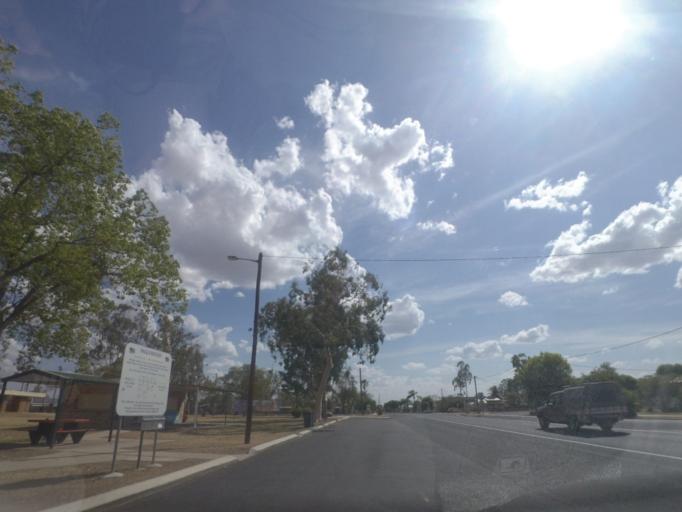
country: AU
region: New South Wales
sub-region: Moree Plains
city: Boggabilla
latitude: -28.4131
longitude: 151.0846
